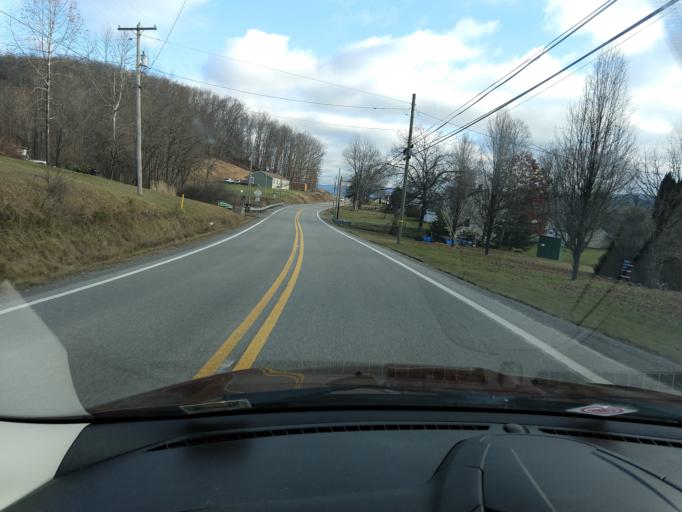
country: US
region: West Virginia
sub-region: Randolph County
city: Elkins
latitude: 38.7730
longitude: -79.9245
